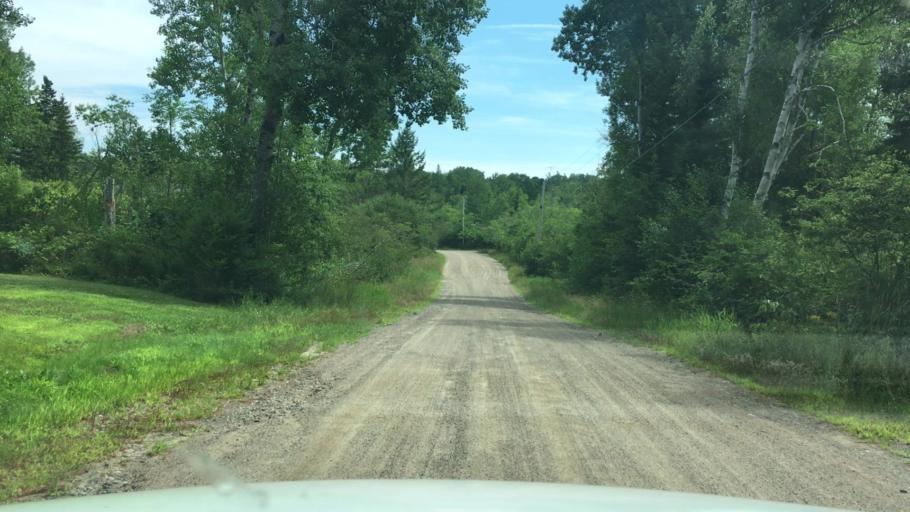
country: CA
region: New Brunswick
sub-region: Charlotte County
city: Saint Andrews
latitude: 45.0361
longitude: -67.1148
